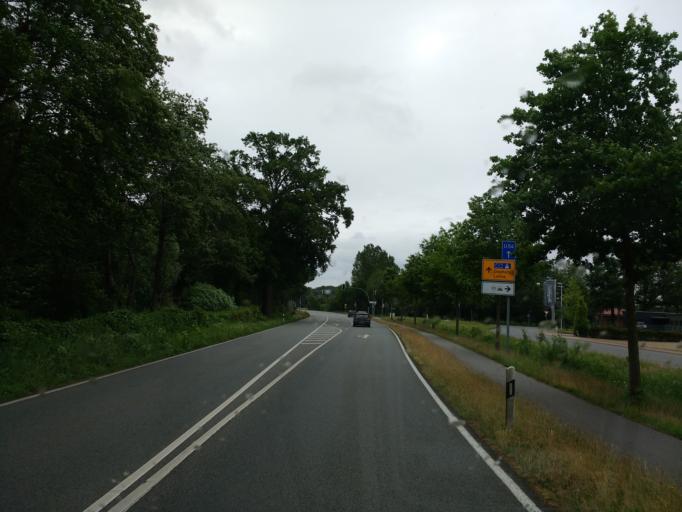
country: DE
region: Lower Saxony
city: Dinklage
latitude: 52.6675
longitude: 8.1418
